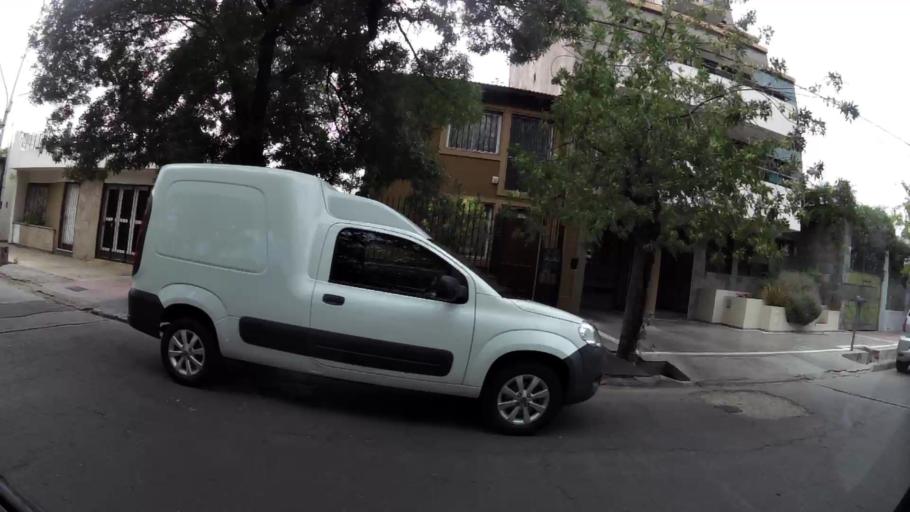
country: AR
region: Mendoza
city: Mendoza
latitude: -32.8976
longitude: -68.8568
